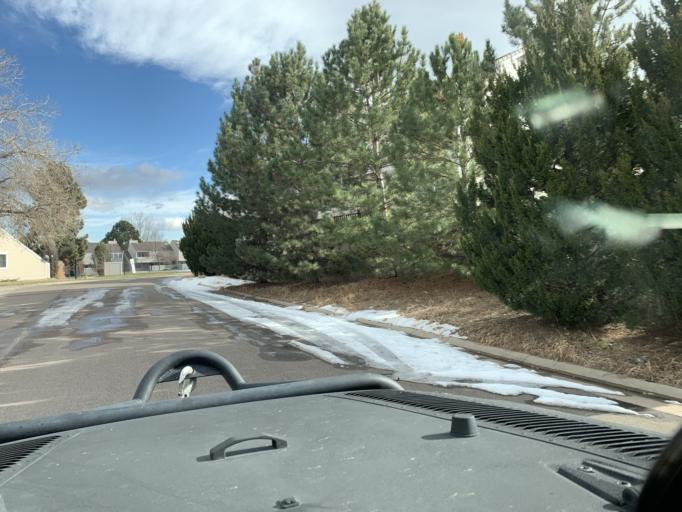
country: US
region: Colorado
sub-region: Adams County
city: Aurora
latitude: 39.7164
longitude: -104.8135
